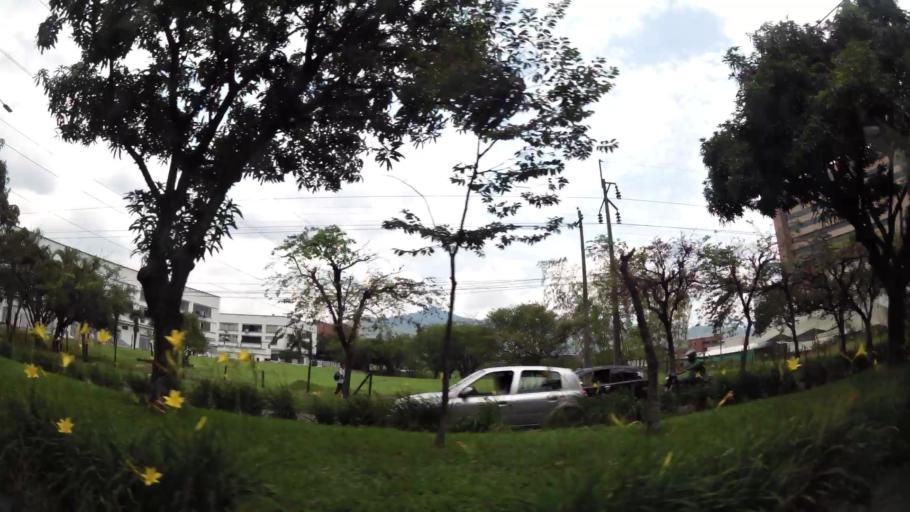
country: CO
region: Antioquia
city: Envigado
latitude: 6.1649
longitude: -75.6008
